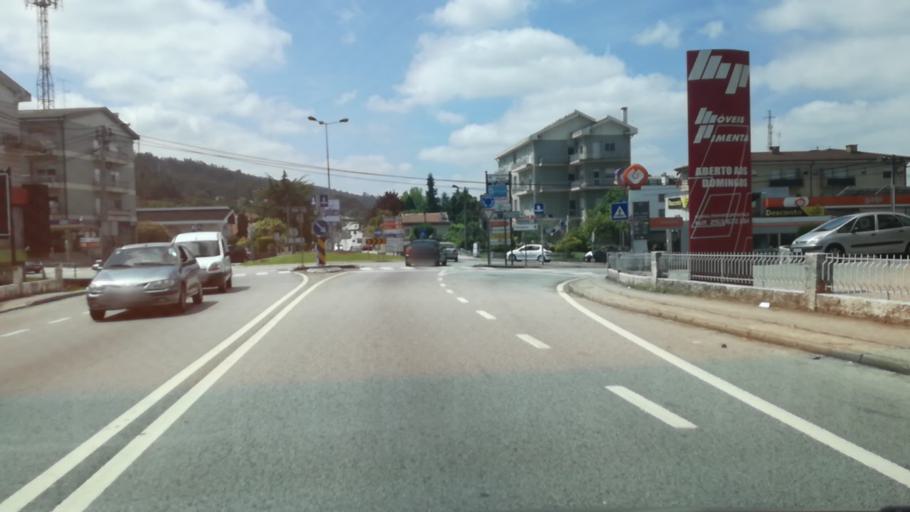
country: PT
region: Braga
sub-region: Braga
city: Oliveira
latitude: 41.5125
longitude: -8.4510
